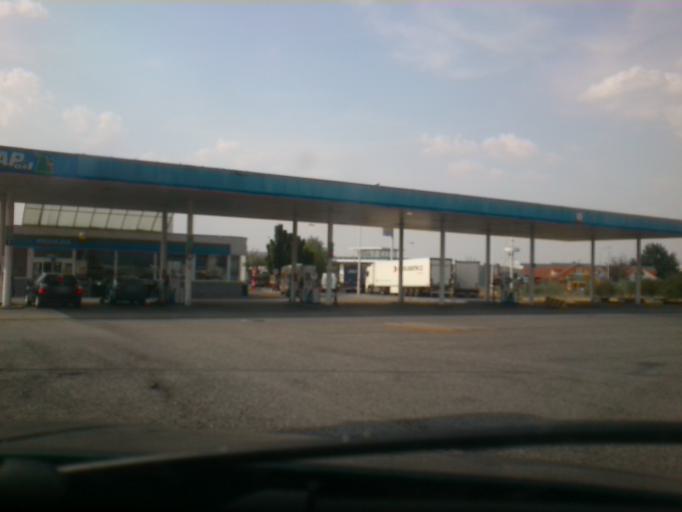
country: CZ
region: Central Bohemia
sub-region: Okres Praha-Zapad
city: Pruhonice
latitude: 50.0034
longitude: 14.5706
